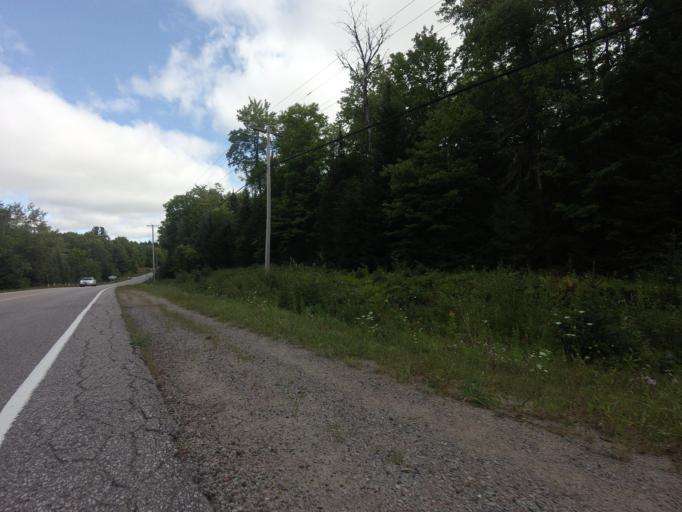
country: CA
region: Ontario
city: Omemee
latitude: 44.7973
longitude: -78.6369
